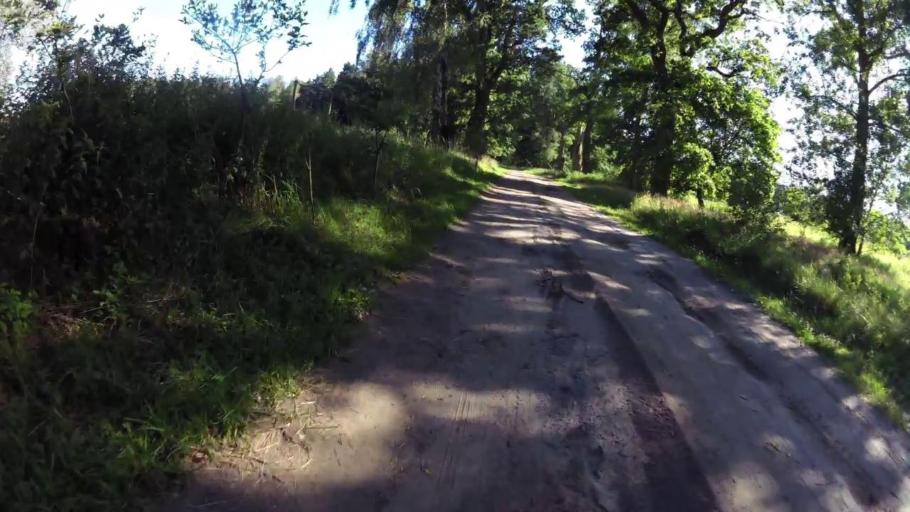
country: PL
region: West Pomeranian Voivodeship
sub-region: Powiat bialogardzki
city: Bialogard
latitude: 53.9876
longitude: 16.0696
